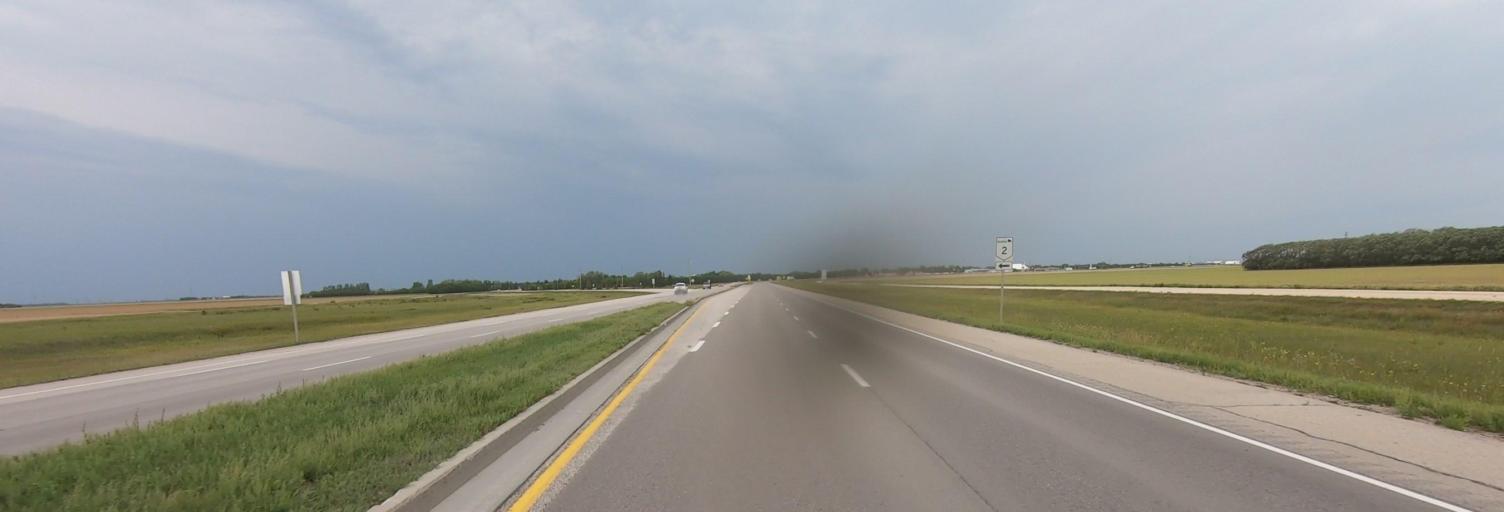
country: CA
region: Manitoba
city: Headingley
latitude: 49.7693
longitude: -97.3009
